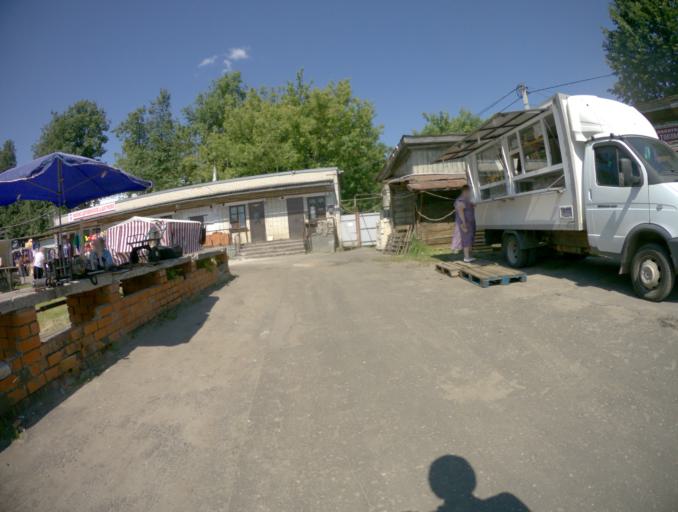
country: RU
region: Vladimir
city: Vyazniki
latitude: 56.2476
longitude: 42.1588
